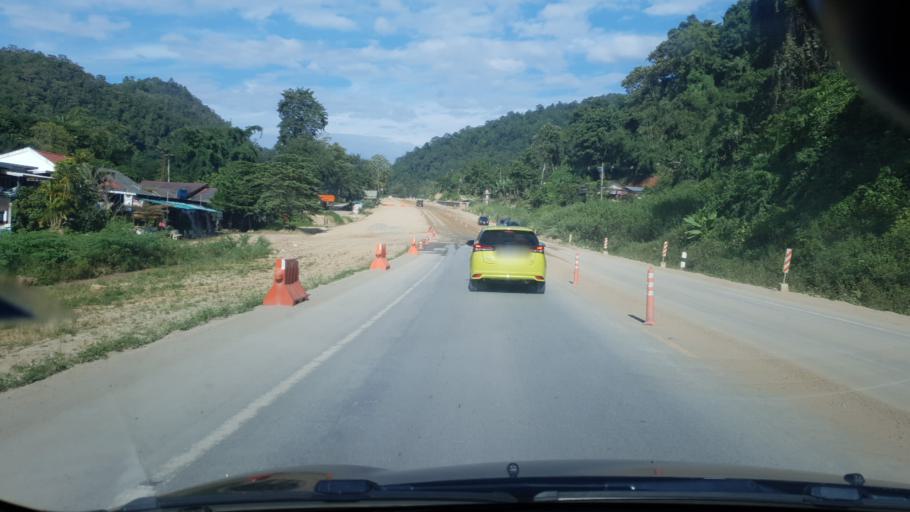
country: TH
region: Chiang Mai
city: Mae On
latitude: 19.0394
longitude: 99.3340
